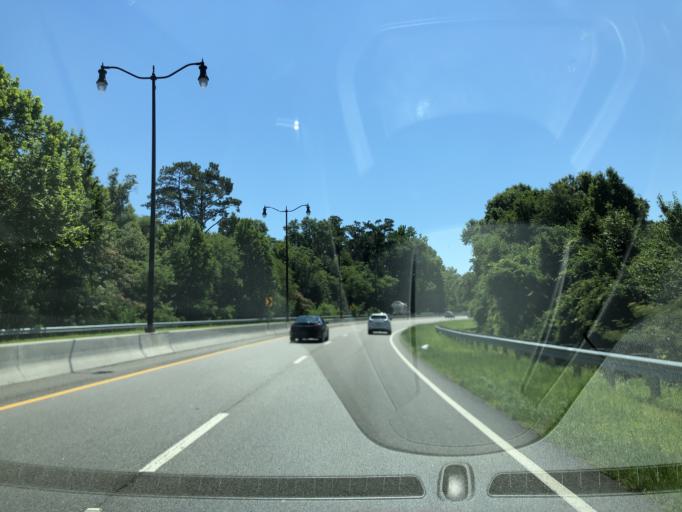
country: US
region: South Carolina
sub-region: Aiken County
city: North Augusta
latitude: 33.5186
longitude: -82.0080
